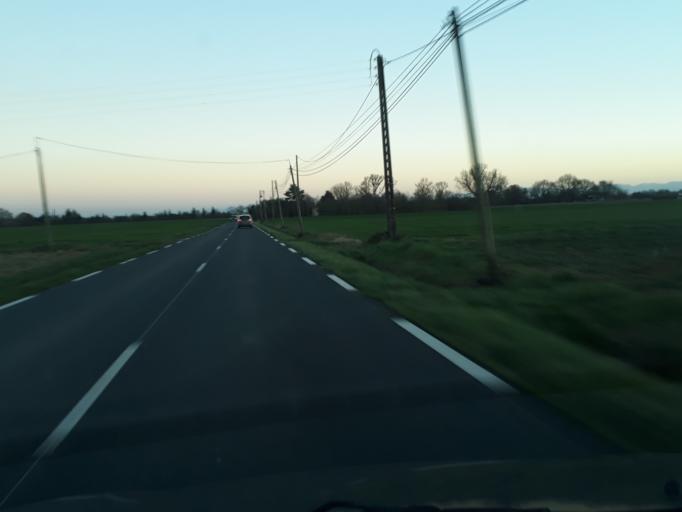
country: FR
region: Midi-Pyrenees
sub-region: Departement de la Haute-Garonne
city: Saint-Lys
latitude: 43.5347
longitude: 1.1672
